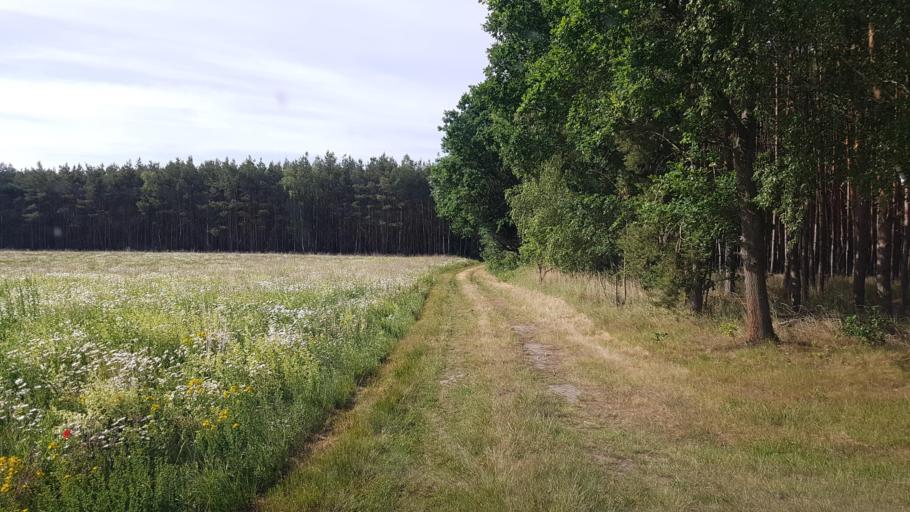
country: DE
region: Brandenburg
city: Plessa
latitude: 51.5307
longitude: 13.6504
